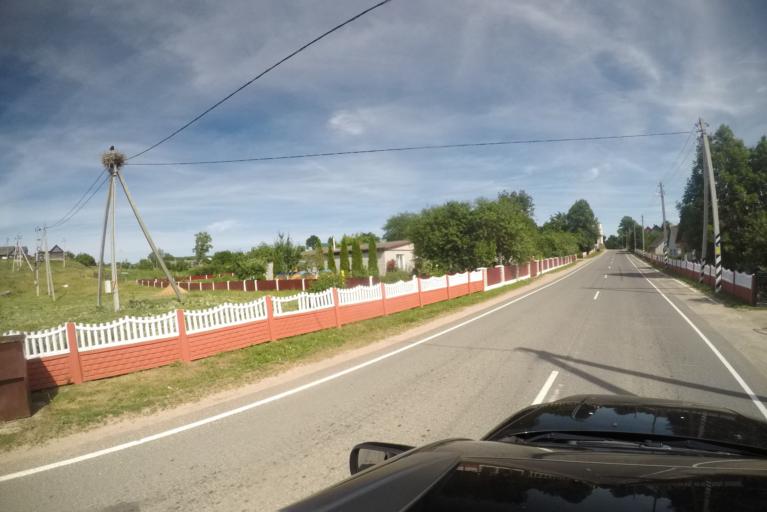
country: BY
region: Grodnenskaya
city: Hal'shany
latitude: 54.2543
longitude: 26.0179
